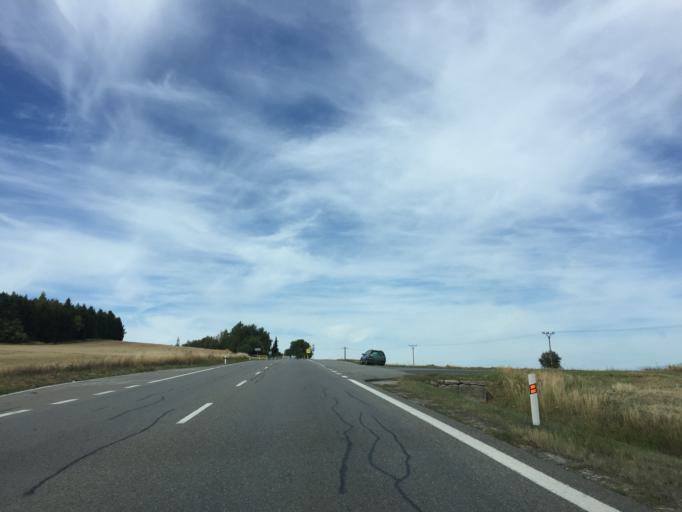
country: CZ
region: Jihocesky
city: Chotoviny
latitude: 49.5516
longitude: 14.6657
